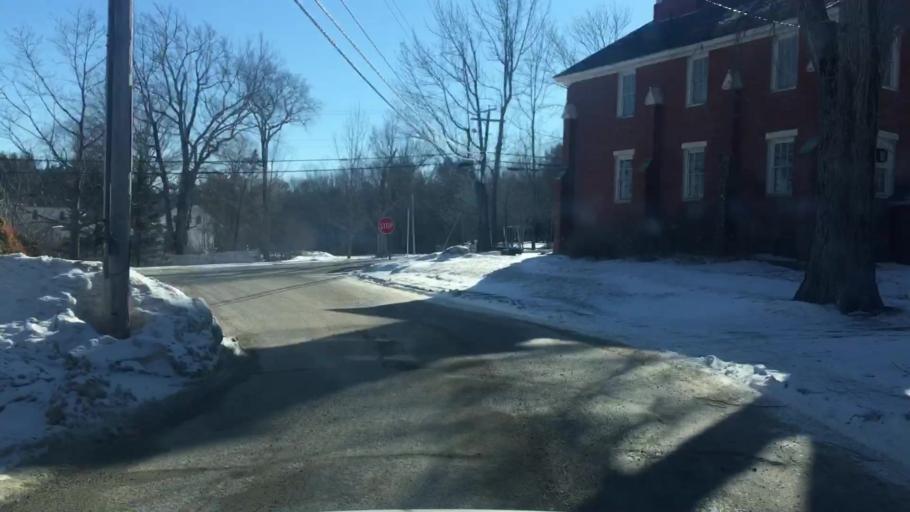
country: US
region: Maine
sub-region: Hancock County
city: Sedgwick
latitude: 44.4122
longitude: -68.5911
